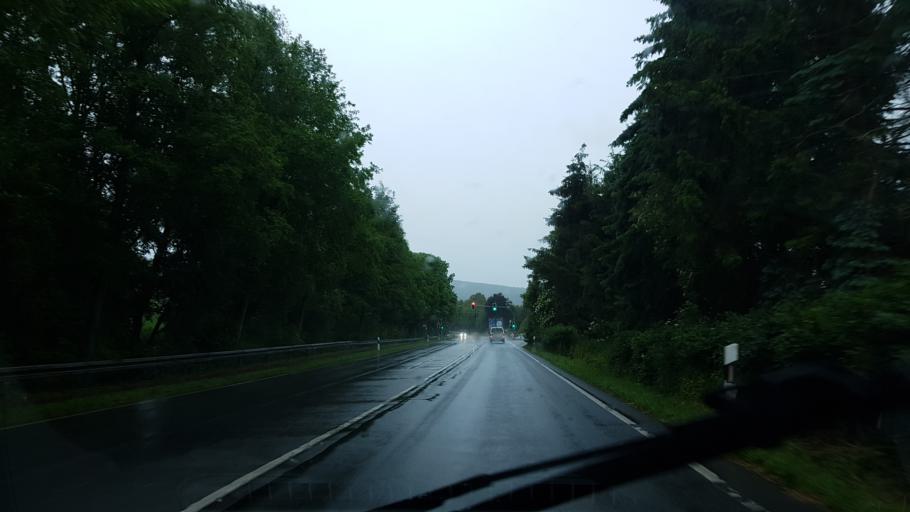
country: DE
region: Lower Saxony
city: Delligsen
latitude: 51.9417
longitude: 9.8215
